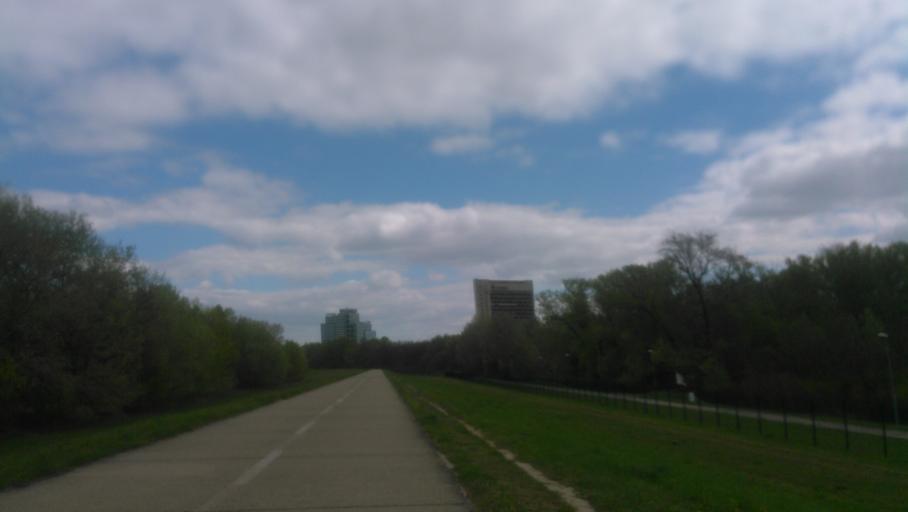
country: SK
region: Bratislavsky
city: Bratislava
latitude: 48.1366
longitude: 17.0891
